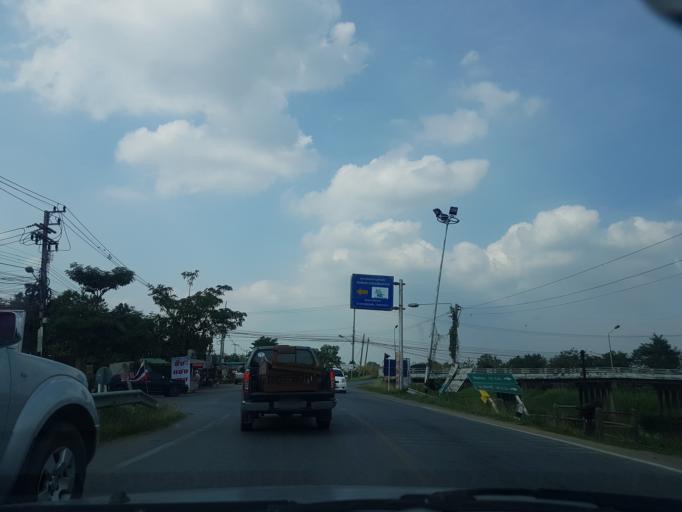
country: TH
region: Phra Nakhon Si Ayutthaya
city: Phachi
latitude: 14.3973
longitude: 100.7928
